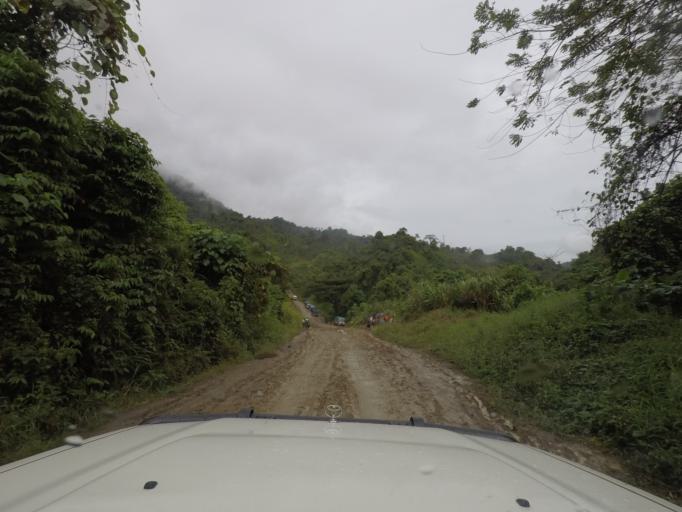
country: PG
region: Madang
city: Madang
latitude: -5.4918
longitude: 145.4816
